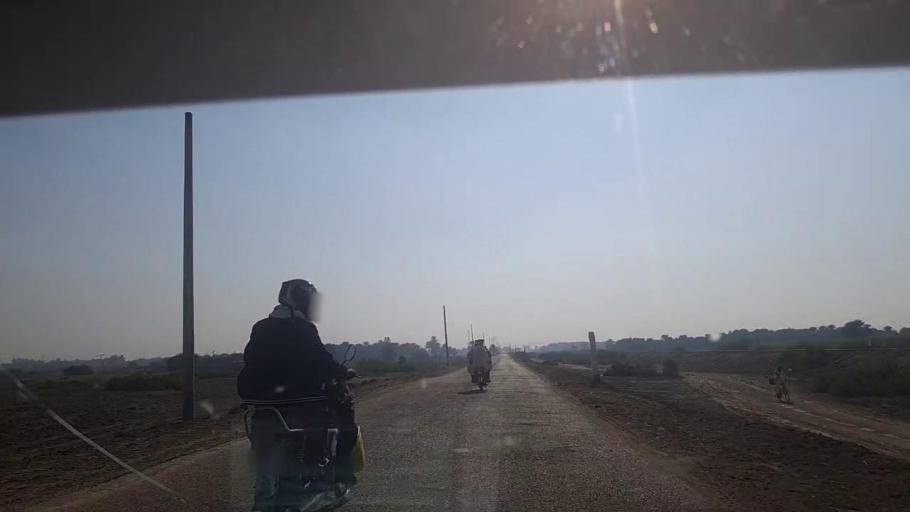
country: PK
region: Sindh
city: Gambat
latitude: 27.3544
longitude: 68.5520
